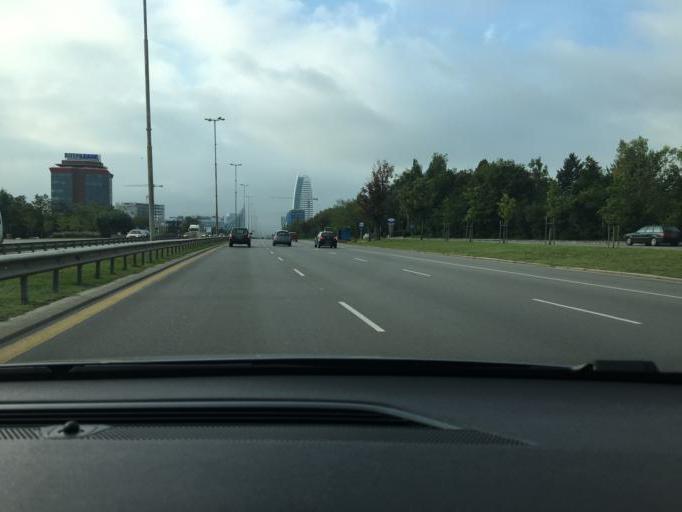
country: BG
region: Sofia-Capital
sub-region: Stolichna Obshtina
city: Sofia
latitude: 42.6547
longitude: 23.3877
